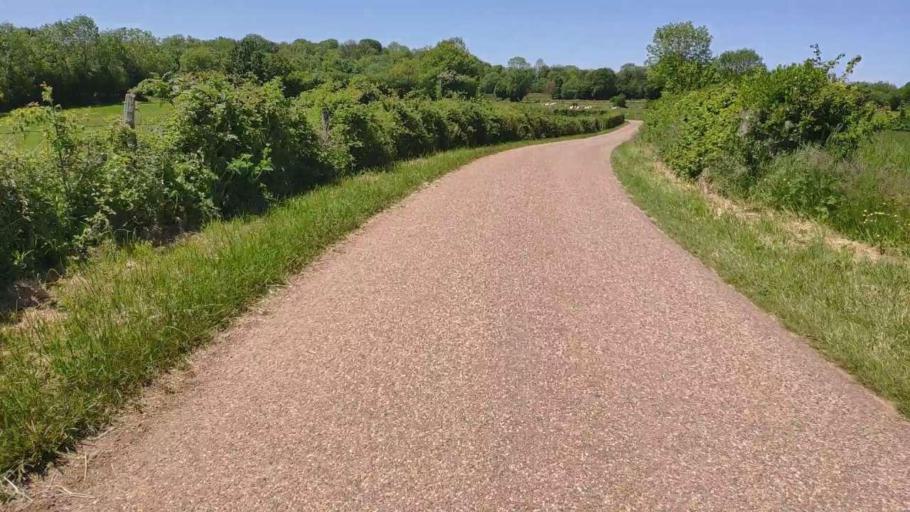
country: FR
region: Franche-Comte
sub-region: Departement du Jura
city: Poligny
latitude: 46.7385
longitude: 5.6831
